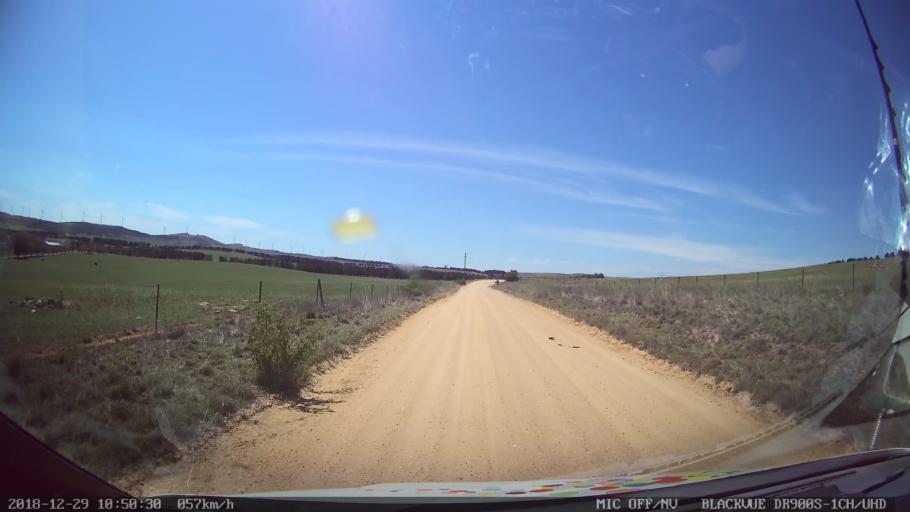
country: AU
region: New South Wales
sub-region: Palerang
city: Bungendore
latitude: -35.0823
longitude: 149.5230
